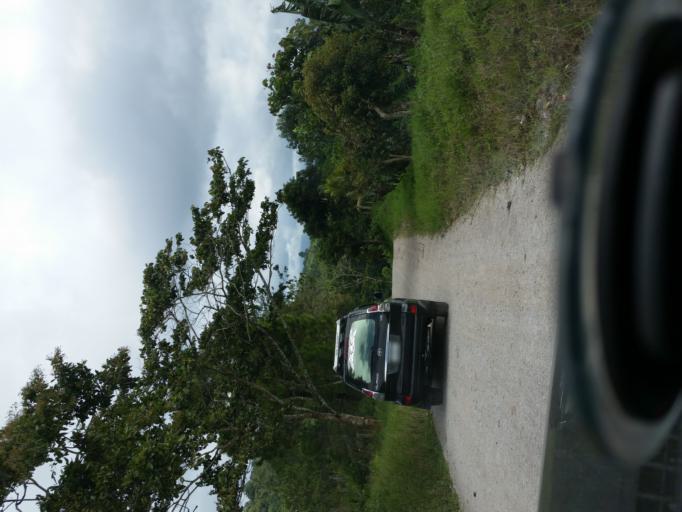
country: NI
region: Jinotega
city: Jinotega
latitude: 13.3000
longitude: -85.8779
